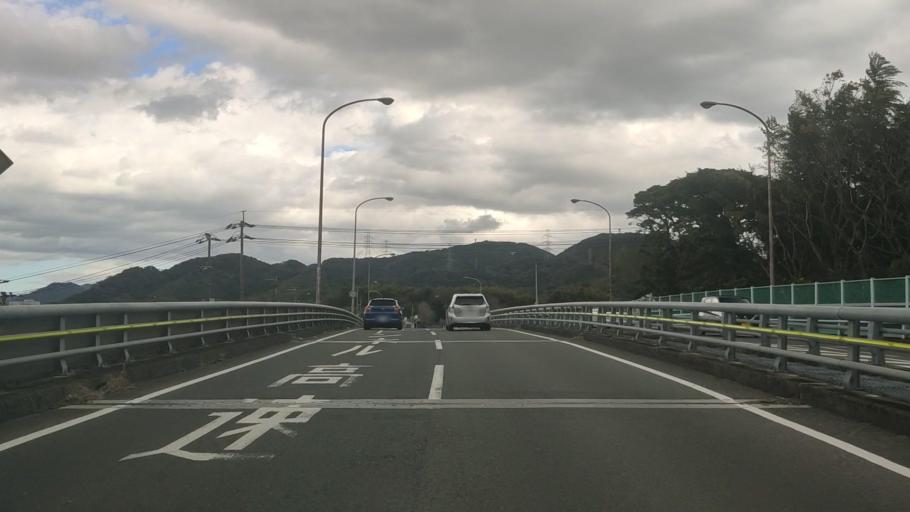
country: JP
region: Yamaguchi
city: Shimonoseki
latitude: 33.9739
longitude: 130.9470
